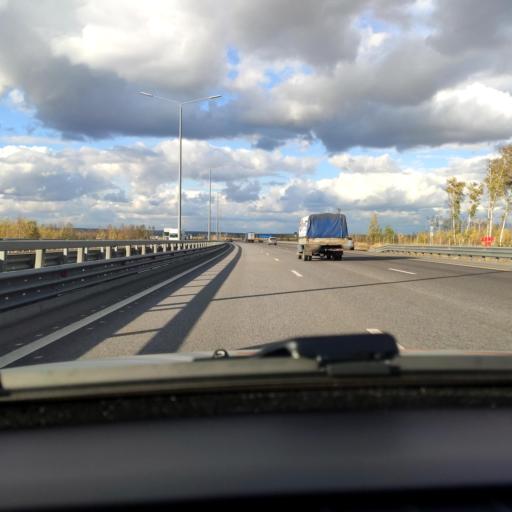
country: RU
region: Voronezj
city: Somovo
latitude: 51.7600
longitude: 39.3071
